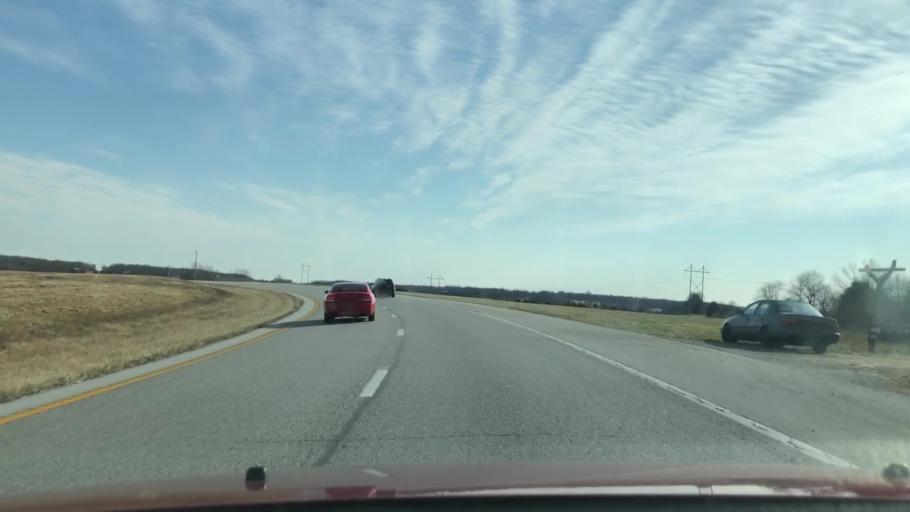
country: US
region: Missouri
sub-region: Webster County
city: Seymour
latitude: 37.1187
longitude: -92.6940
